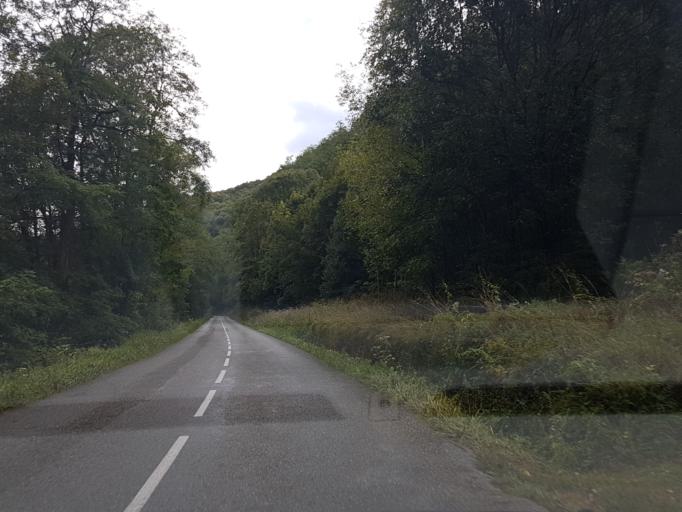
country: FR
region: Midi-Pyrenees
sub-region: Departement de l'Ariege
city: Saint-Girons
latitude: 42.9062
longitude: 1.2190
